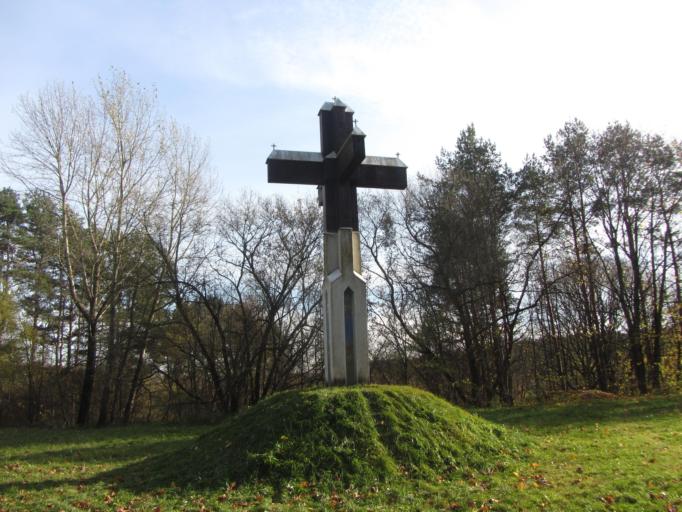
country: LT
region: Vilnius County
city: Seskine
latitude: 54.6938
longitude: 25.2376
